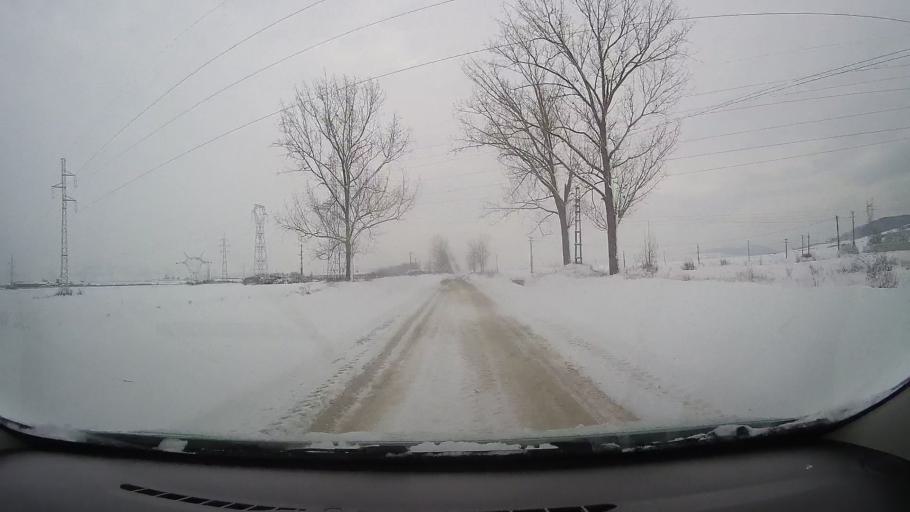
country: RO
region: Alba
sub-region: Comuna Pianu
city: Pianu de Jos
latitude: 45.9619
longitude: 23.5068
